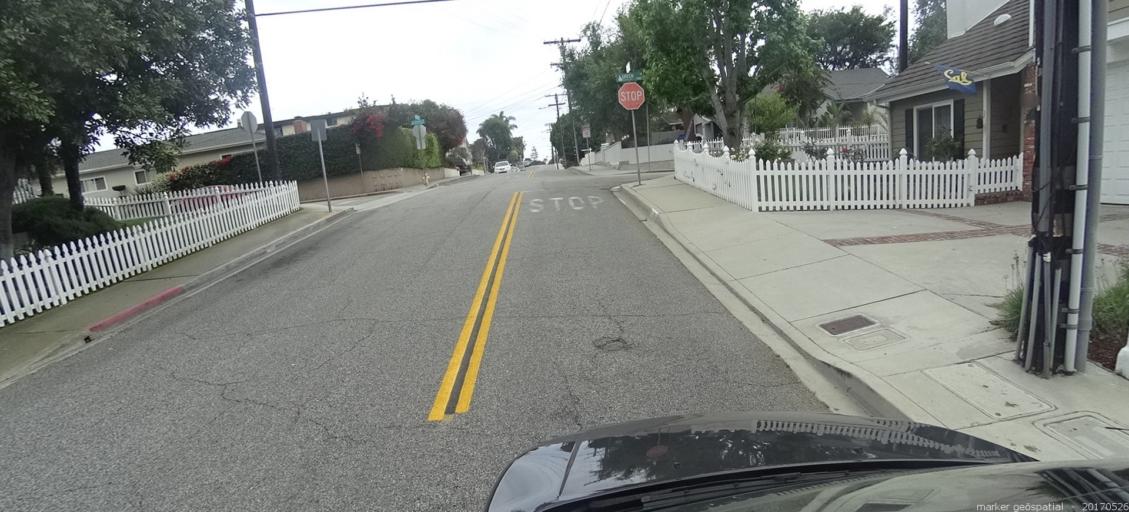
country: US
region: California
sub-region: Los Angeles County
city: Lawndale
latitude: 33.8766
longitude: -118.3767
